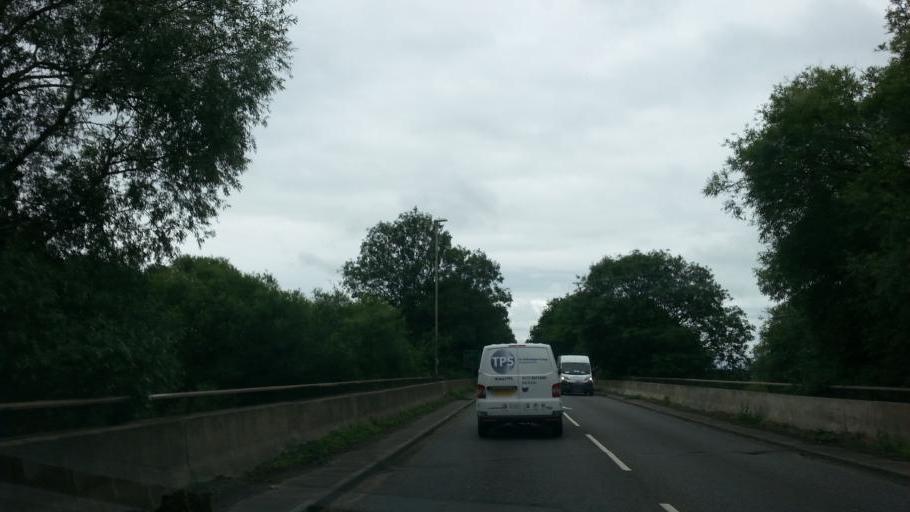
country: GB
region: England
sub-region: Wiltshire
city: Melksham
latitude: 51.3738
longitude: -2.1449
